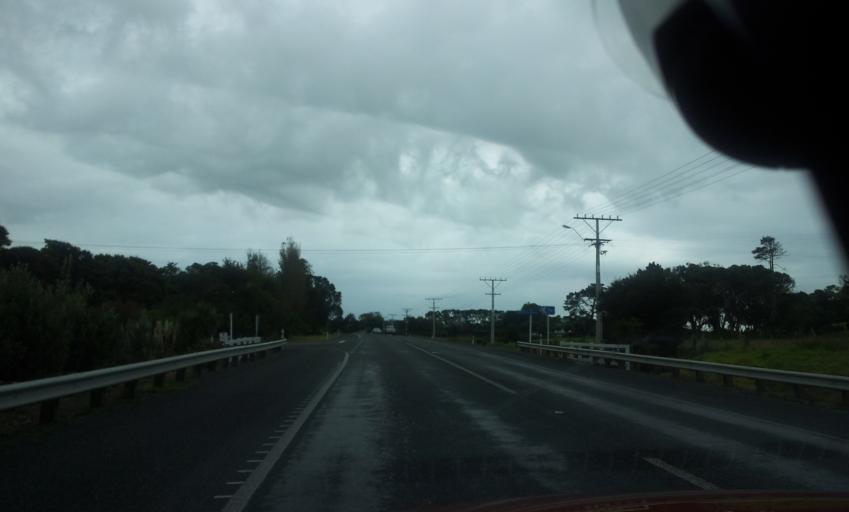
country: NZ
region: Northland
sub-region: Whangarei
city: Ruakaka
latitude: -35.9155
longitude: 174.4518
